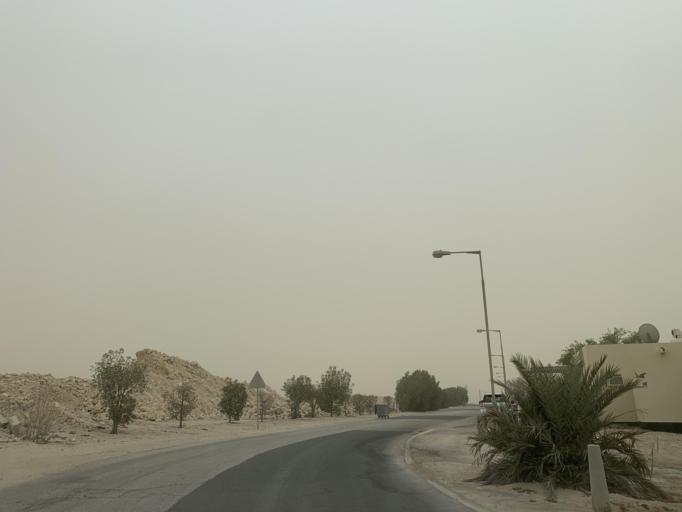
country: BH
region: Central Governorate
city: Madinat Hamad
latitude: 26.1328
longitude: 50.5219
